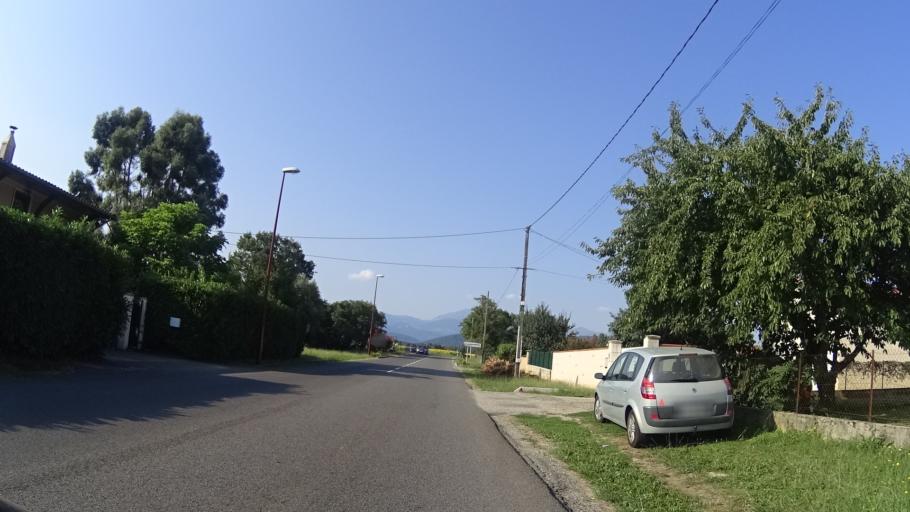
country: FR
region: Midi-Pyrenees
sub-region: Departement de l'Ariege
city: Lavelanet
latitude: 42.9946
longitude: 1.8783
